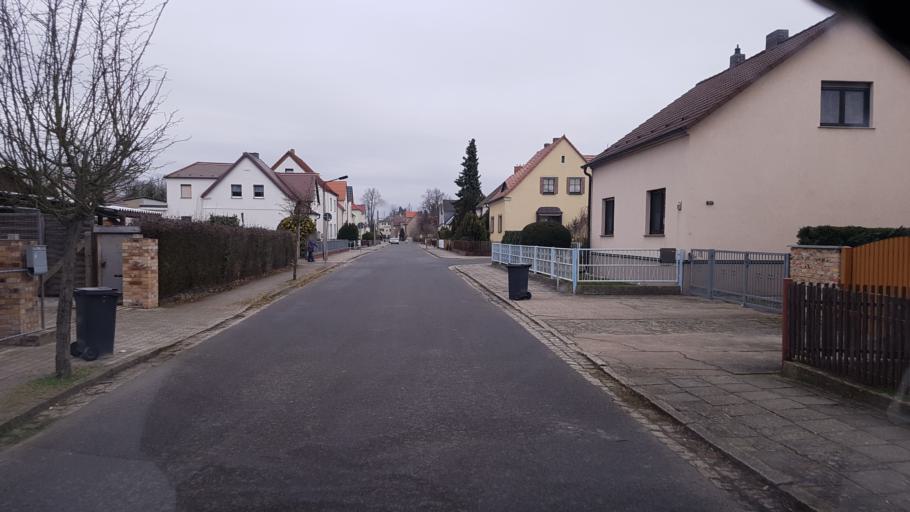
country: DE
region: Brandenburg
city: Ruhland
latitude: 51.4542
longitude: 13.8622
